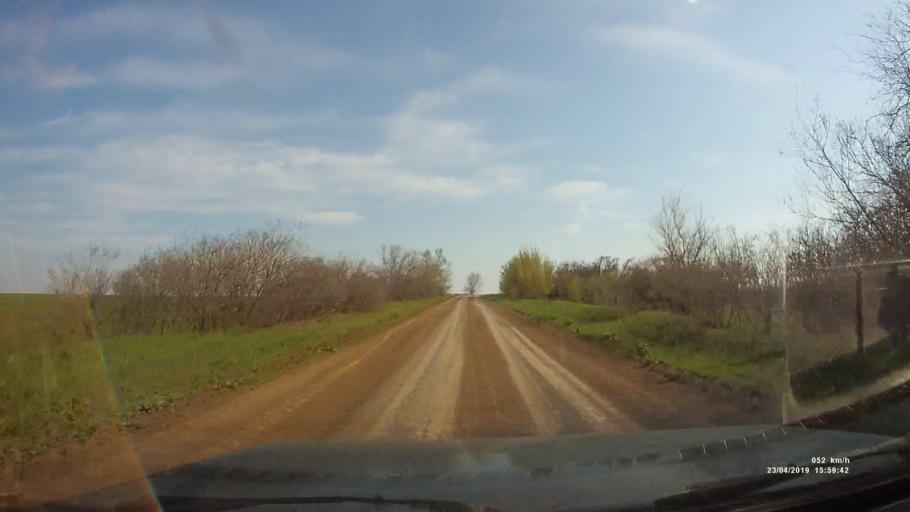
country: RU
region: Rostov
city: Remontnoye
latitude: 46.5148
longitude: 43.1096
